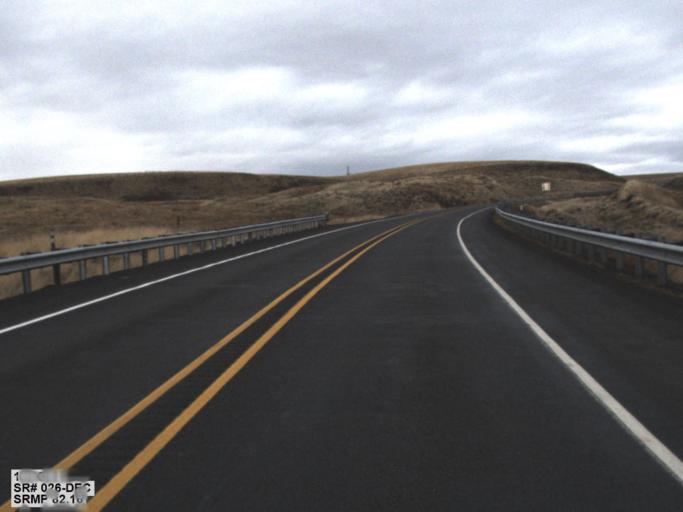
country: US
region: Washington
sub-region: Adams County
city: Ritzville
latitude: 46.7597
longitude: -118.3249
